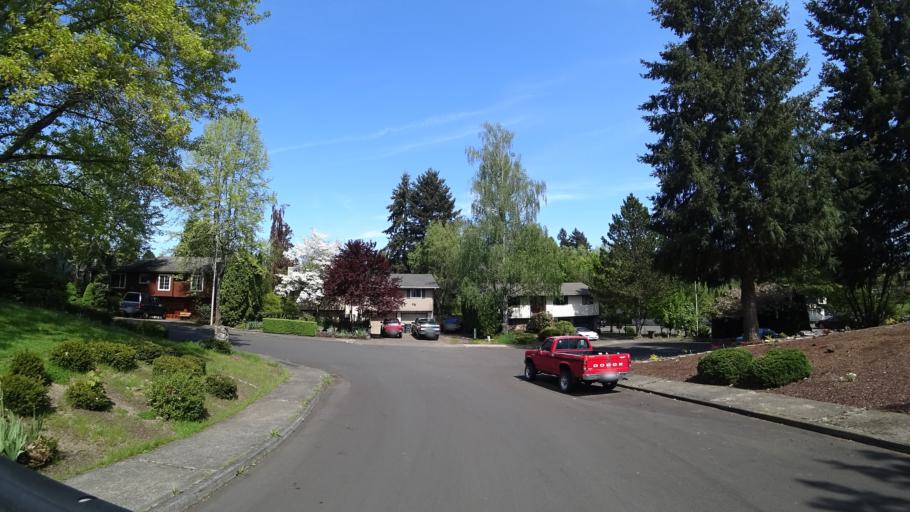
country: US
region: Oregon
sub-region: Washington County
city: Hillsboro
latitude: 45.5094
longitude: -122.9512
